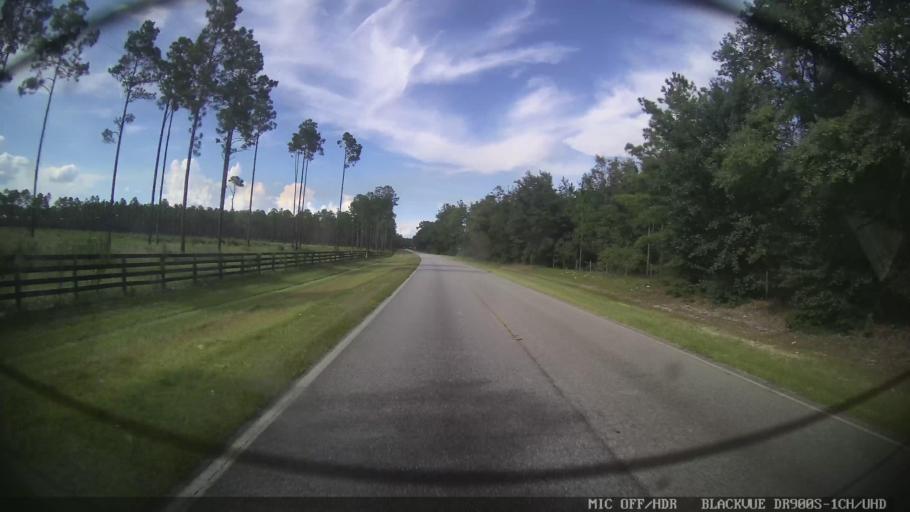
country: US
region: Georgia
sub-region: Echols County
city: Statenville
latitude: 30.6314
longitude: -83.1965
